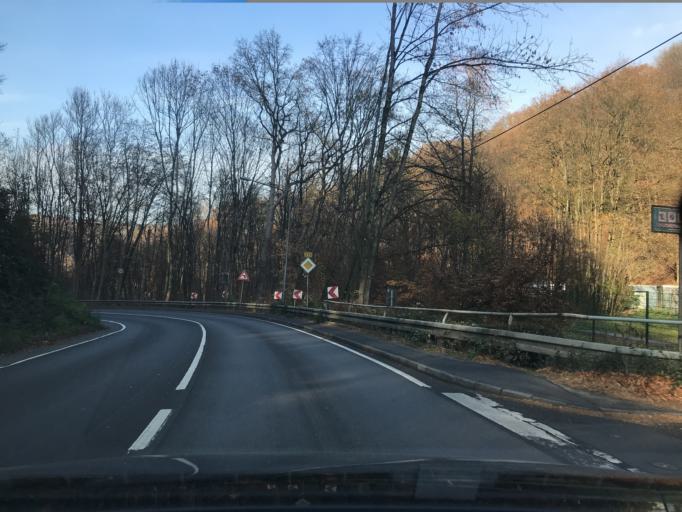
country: DE
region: North Rhine-Westphalia
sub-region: Regierungsbezirk Dusseldorf
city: Remscheid
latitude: 51.1711
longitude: 7.1547
